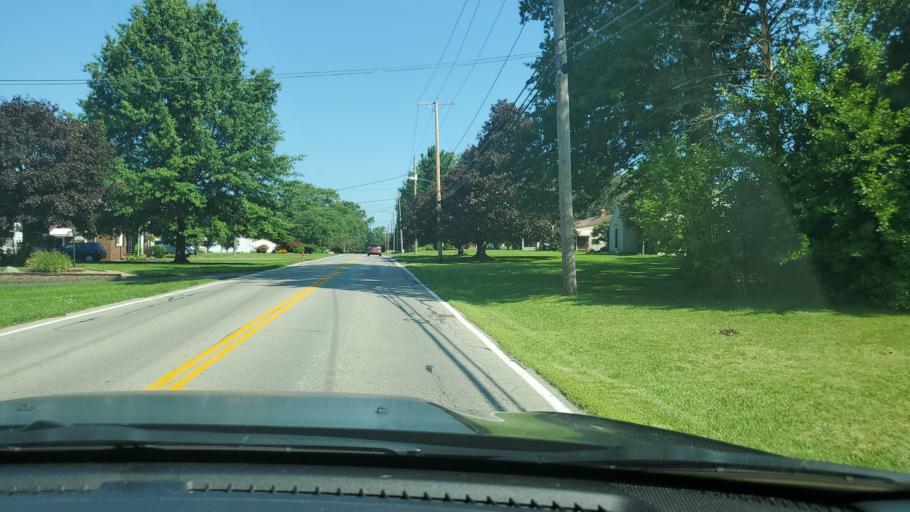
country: US
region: Ohio
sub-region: Trumbull County
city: Girard
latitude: 41.1631
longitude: -80.6893
